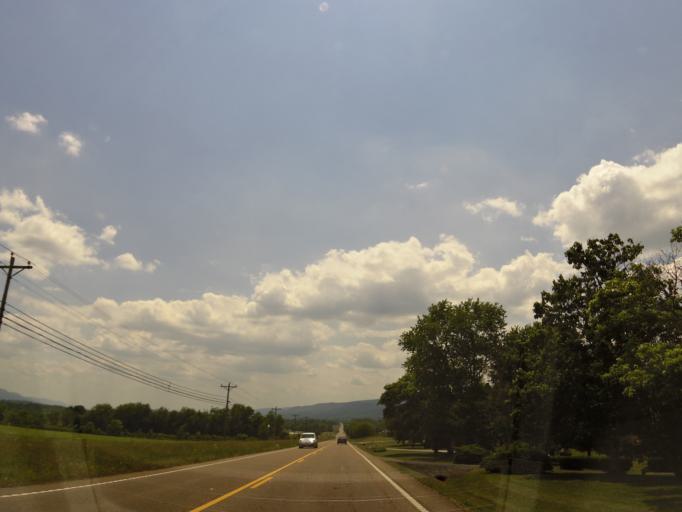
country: US
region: Tennessee
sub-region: Bledsoe County
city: Pikeville
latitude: 35.5911
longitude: -85.2034
